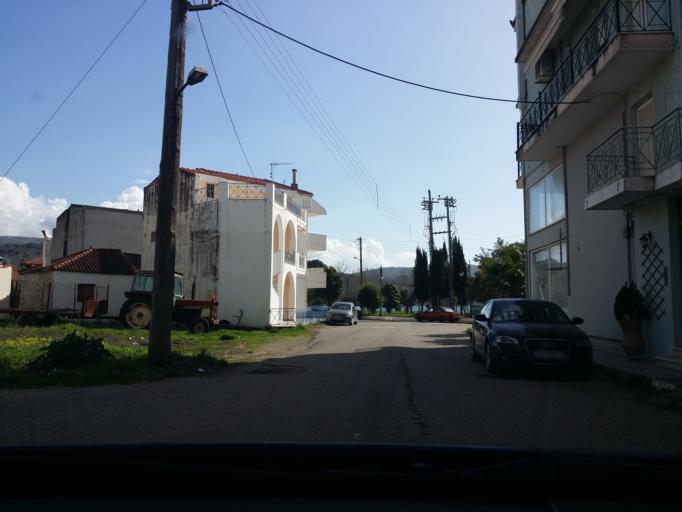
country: GR
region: West Greece
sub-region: Nomos Aitolias kai Akarnanias
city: Astakos
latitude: 38.5360
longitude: 21.0864
